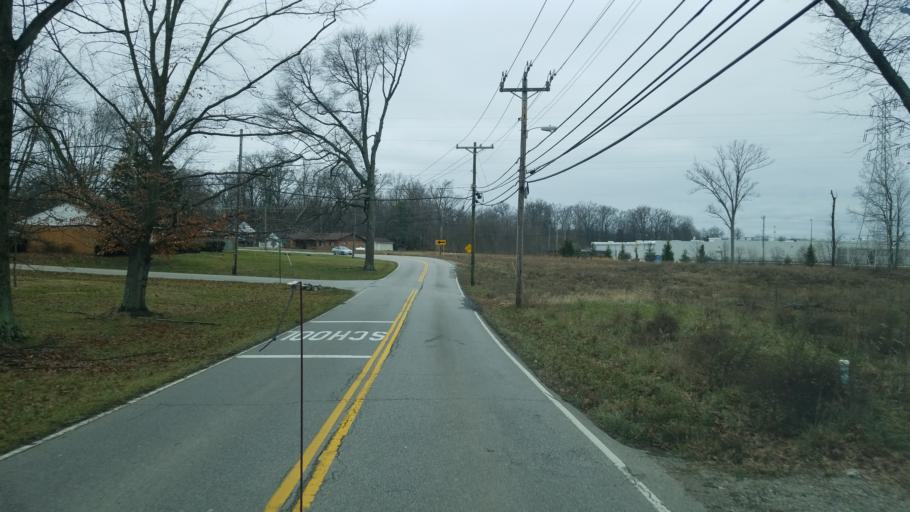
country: US
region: Ohio
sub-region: Clermont County
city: Summerside
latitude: 39.0886
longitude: -84.2663
